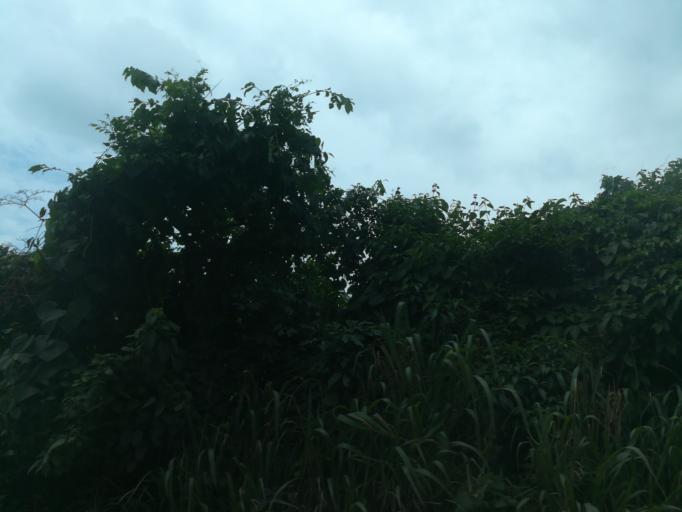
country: NG
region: Lagos
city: Ejirin
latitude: 6.6438
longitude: 3.8531
